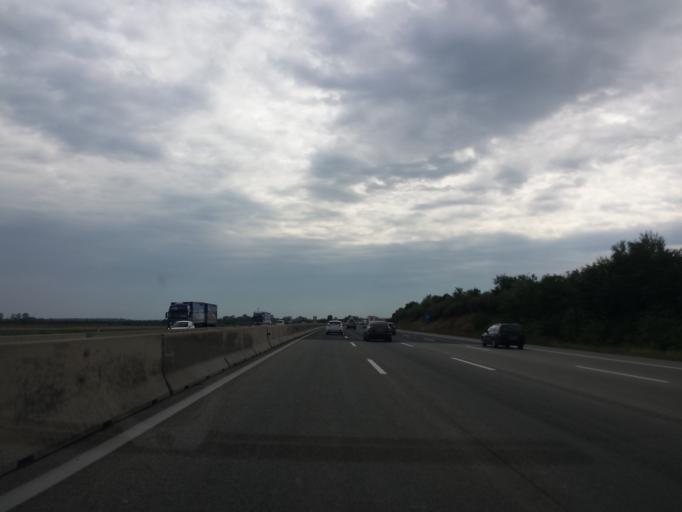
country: AT
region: Lower Austria
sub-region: Politischer Bezirk Modling
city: Guntramsdorf
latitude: 48.0249
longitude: 16.3335
